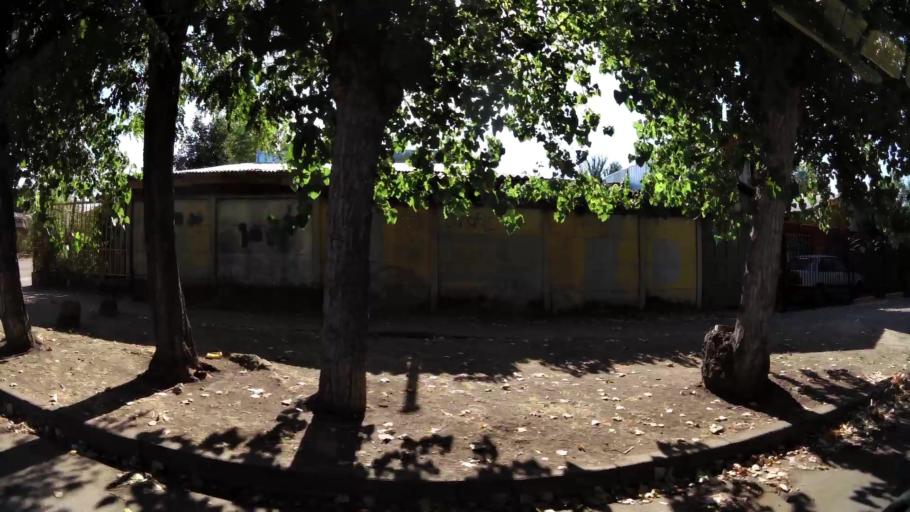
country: CL
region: Maule
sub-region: Provincia de Talca
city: Talca
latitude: -35.4421
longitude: -71.6512
